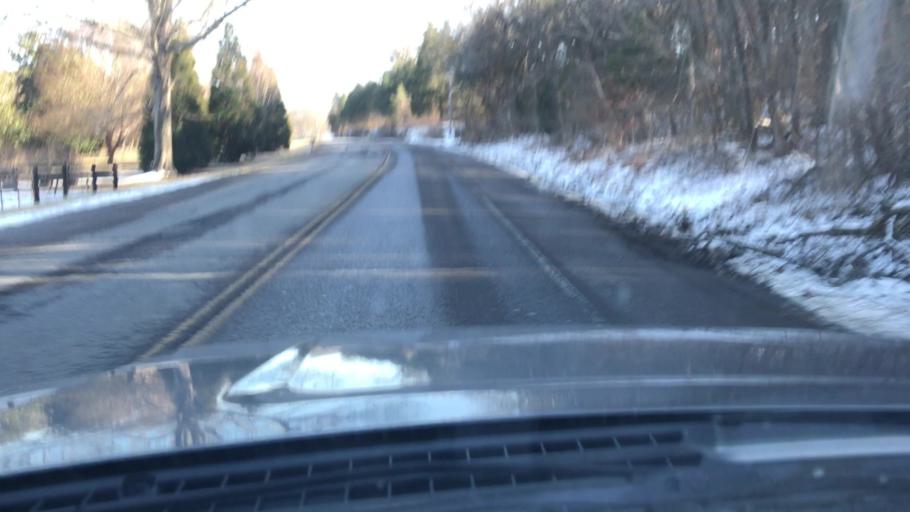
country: US
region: Tennessee
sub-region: Davidson County
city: Forest Hills
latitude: 36.0270
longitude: -86.8547
